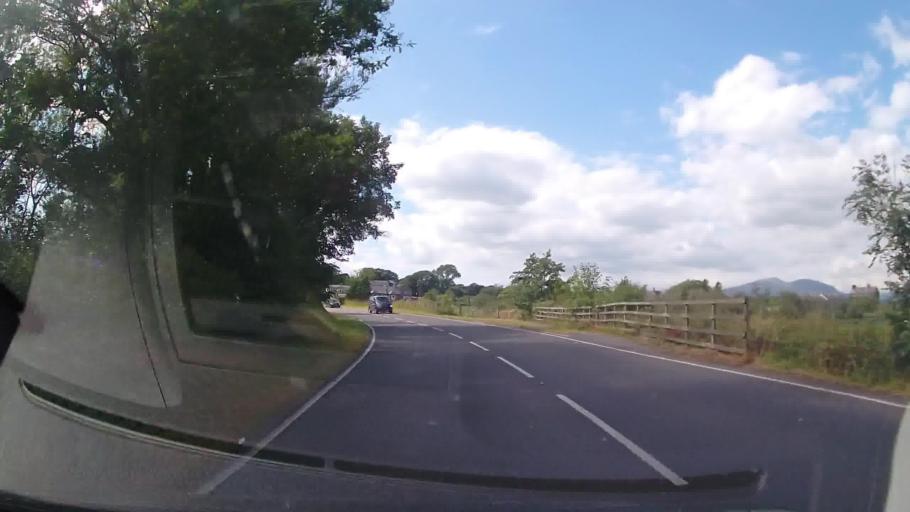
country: GB
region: Wales
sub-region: Gwynedd
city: Penrhyndeudraeth
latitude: 52.8963
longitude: -4.0826
